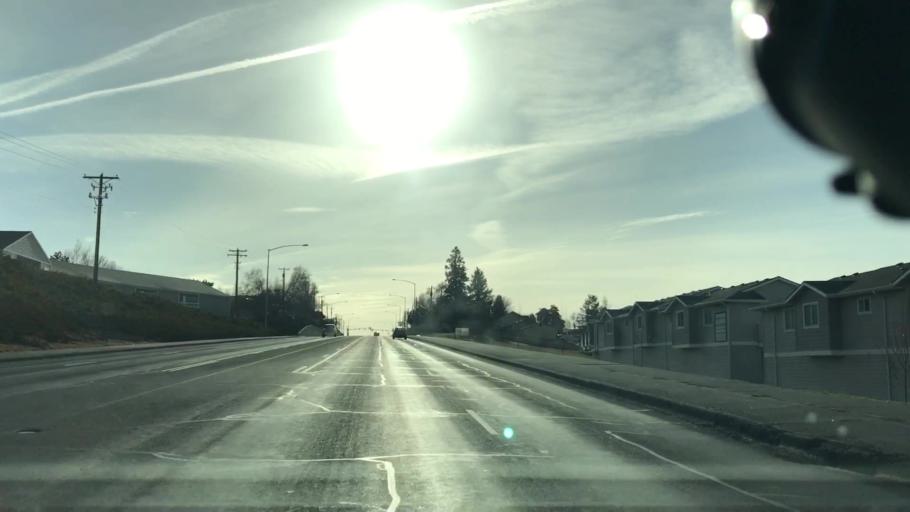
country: US
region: Washington
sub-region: Grant County
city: Moses Lake
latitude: 47.1255
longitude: -119.2688
